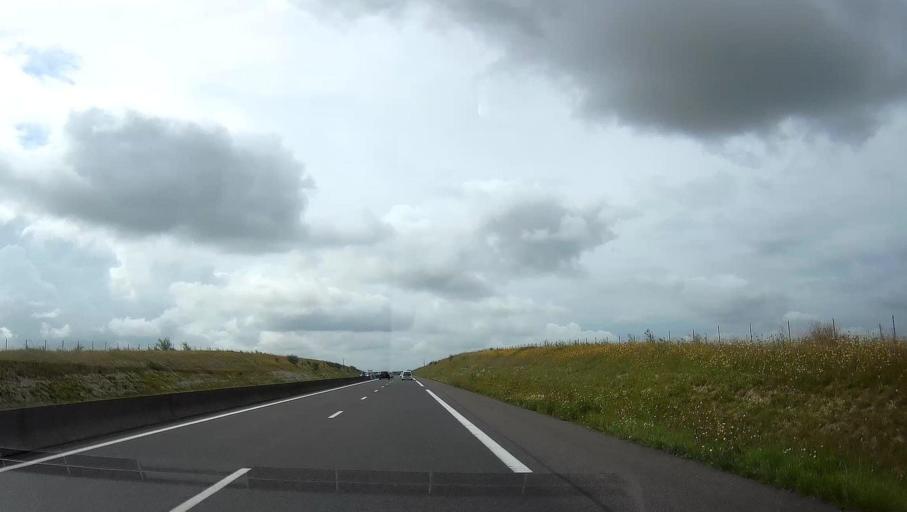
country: FR
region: Champagne-Ardenne
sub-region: Departement de la Marne
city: Compertrix
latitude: 48.8670
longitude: 4.2870
